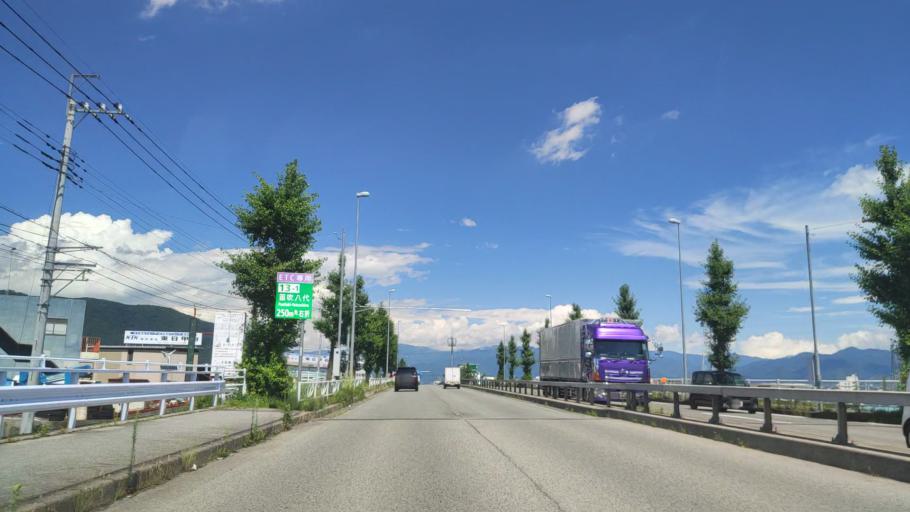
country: JP
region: Yamanashi
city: Kofu-shi
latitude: 35.6401
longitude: 138.5919
